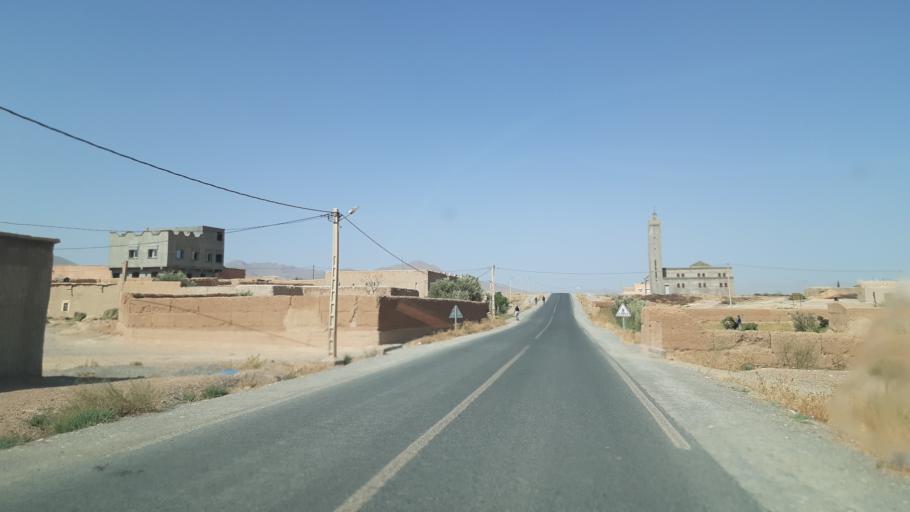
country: MA
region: Meknes-Tafilalet
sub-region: Errachidia
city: Amouguer
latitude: 32.2383
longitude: -4.6095
